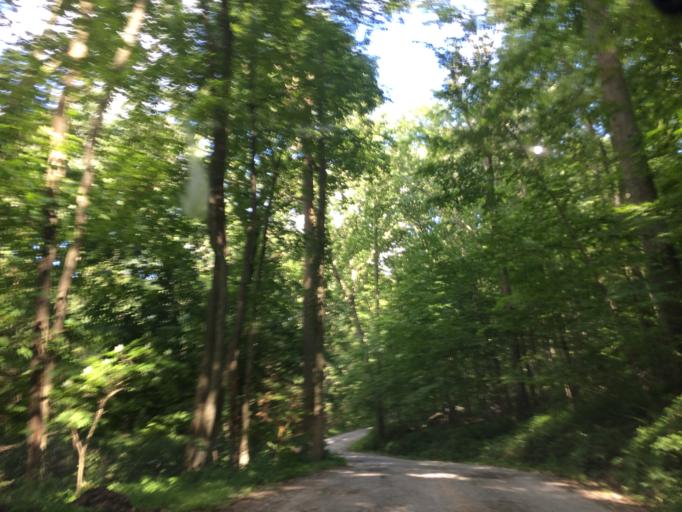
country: US
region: Maryland
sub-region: Washington County
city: Smithsburg
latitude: 39.6582
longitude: -77.5454
